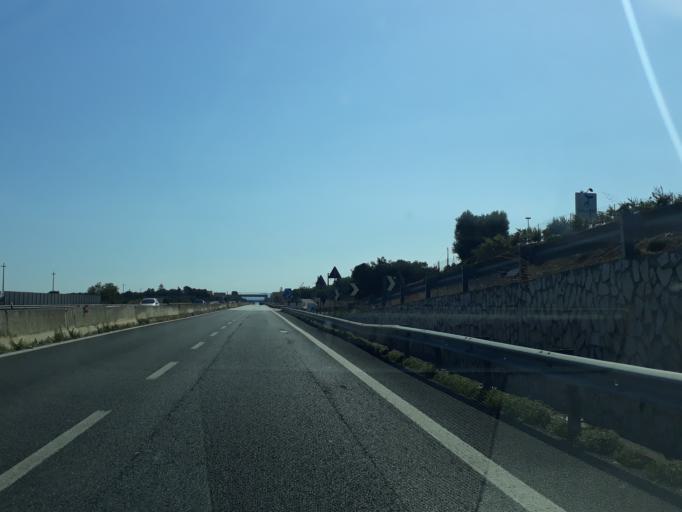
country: IT
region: Apulia
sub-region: Provincia di Brindisi
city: Fasano
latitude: 40.8894
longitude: 17.3334
